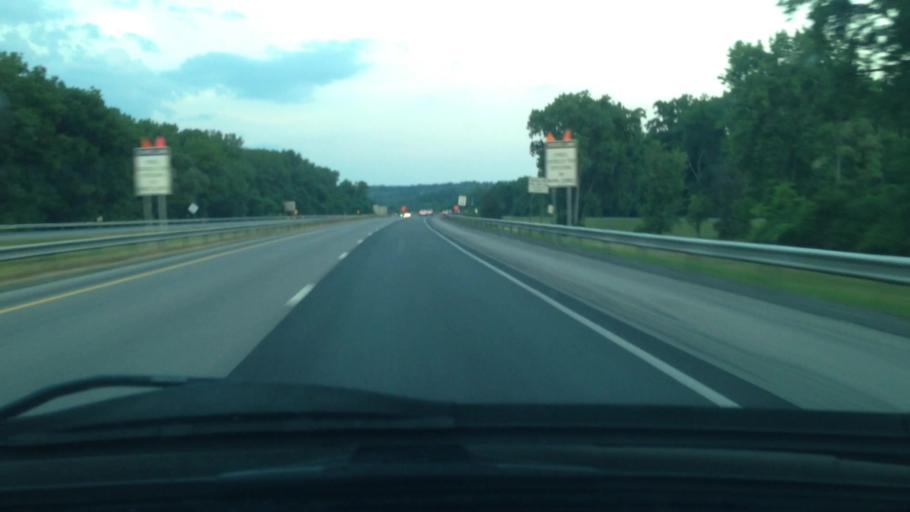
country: US
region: New York
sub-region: Montgomery County
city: Canajoharie
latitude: 42.9023
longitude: -74.5482
